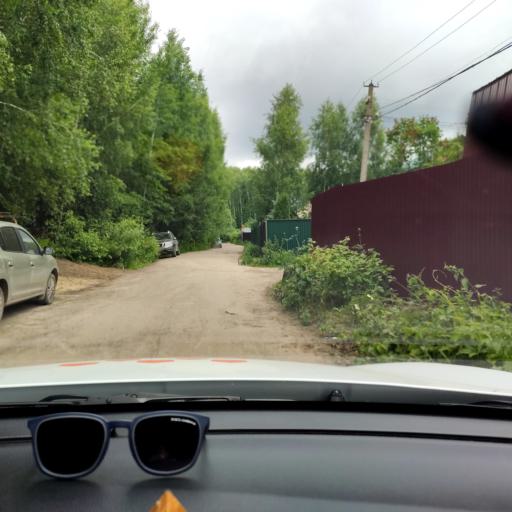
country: RU
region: Tatarstan
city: Vysokaya Gora
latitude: 55.9277
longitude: 49.1616
